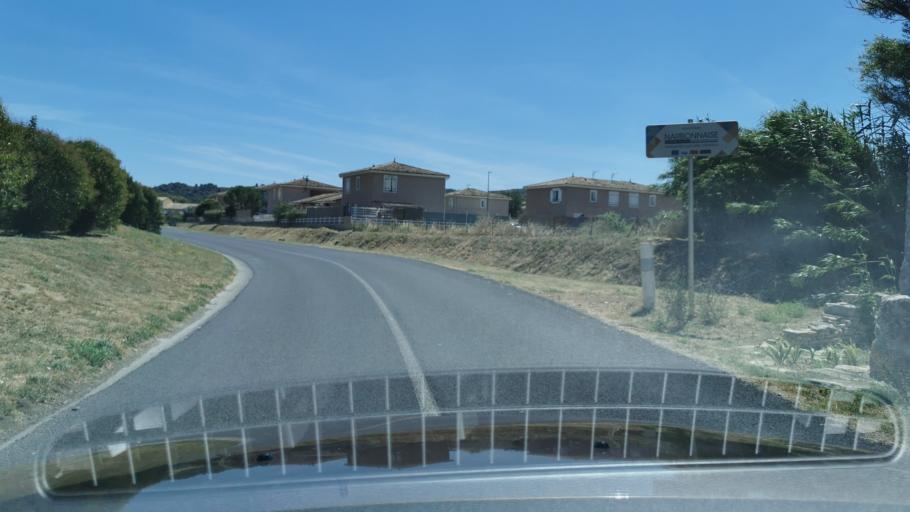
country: FR
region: Languedoc-Roussillon
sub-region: Departement de l'Aude
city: Armissan
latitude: 43.1892
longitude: 3.0853
